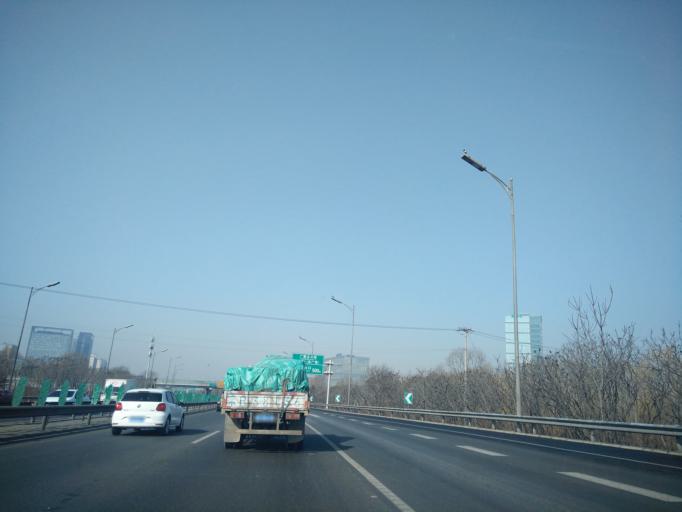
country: CN
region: Beijing
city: Wangjing
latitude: 40.0135
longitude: 116.4752
